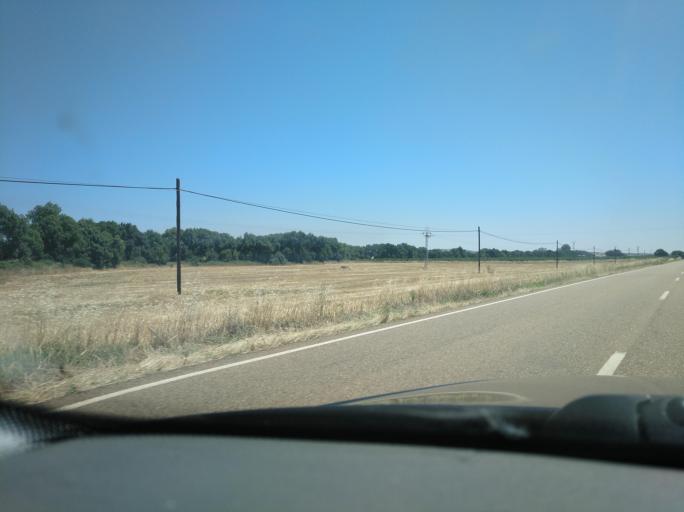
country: ES
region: Extremadura
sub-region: Provincia de Badajoz
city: Olivenza
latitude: 38.7055
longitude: -7.1735
